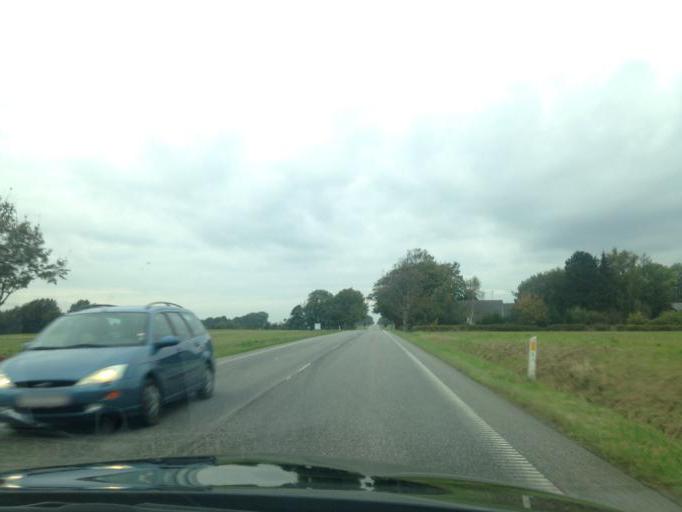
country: DK
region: South Denmark
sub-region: Kolding Kommune
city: Christiansfeld
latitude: 55.4161
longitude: 9.4772
